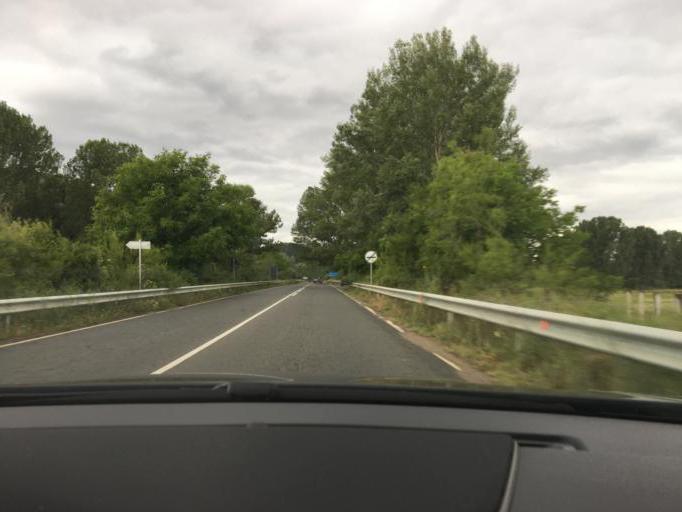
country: BG
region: Kyustendil
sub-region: Obshtina Kyustendil
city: Kyustendil
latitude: 42.2579
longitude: 22.8530
